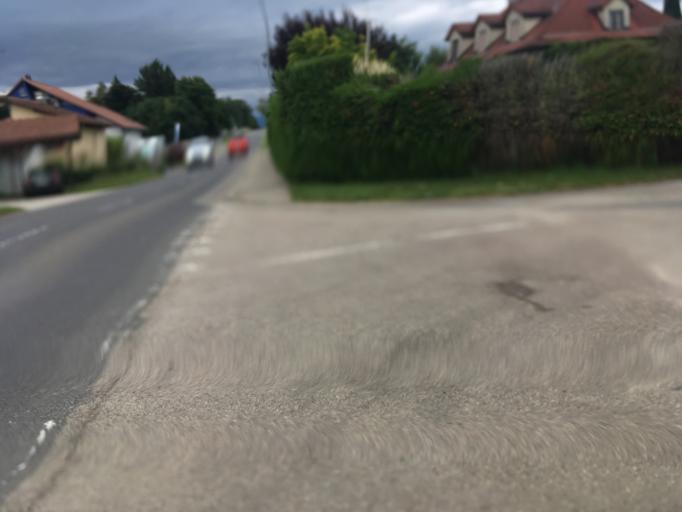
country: CH
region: Vaud
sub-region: Broye-Vully District
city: Payerne
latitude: 46.8758
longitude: 6.9262
